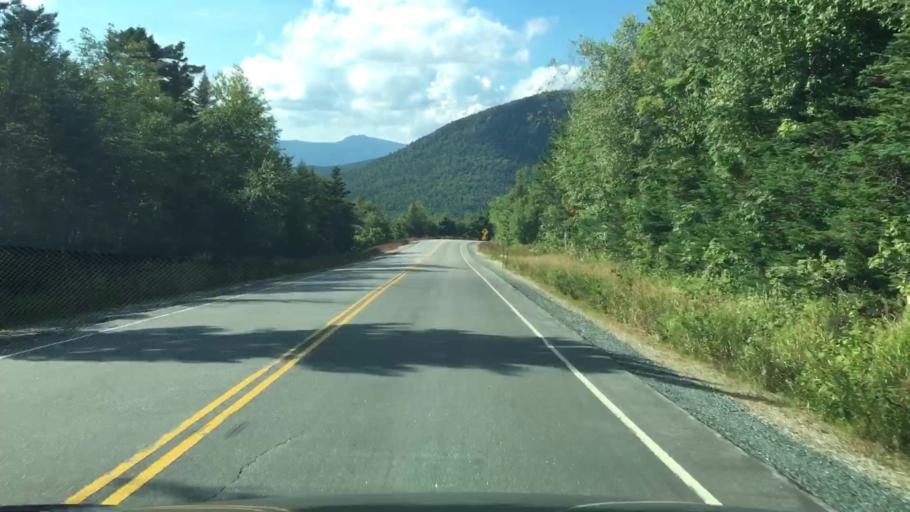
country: US
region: New Hampshire
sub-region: Grafton County
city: Woodstock
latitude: 44.0283
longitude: -71.4963
